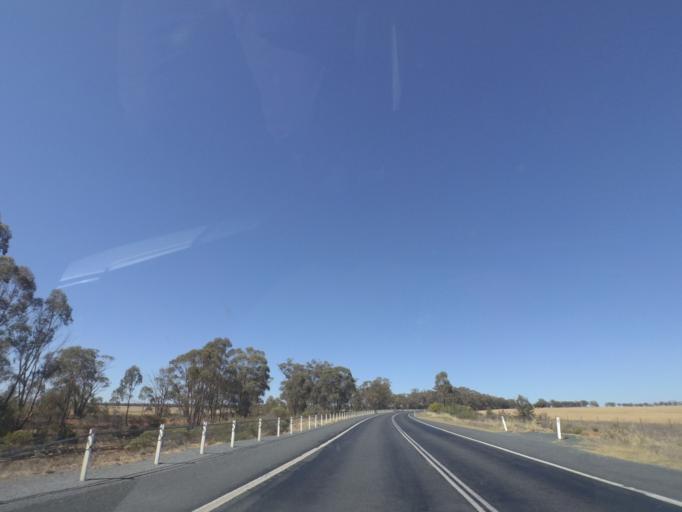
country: AU
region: New South Wales
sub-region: Bland
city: West Wyalong
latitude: -34.1125
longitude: 147.1390
